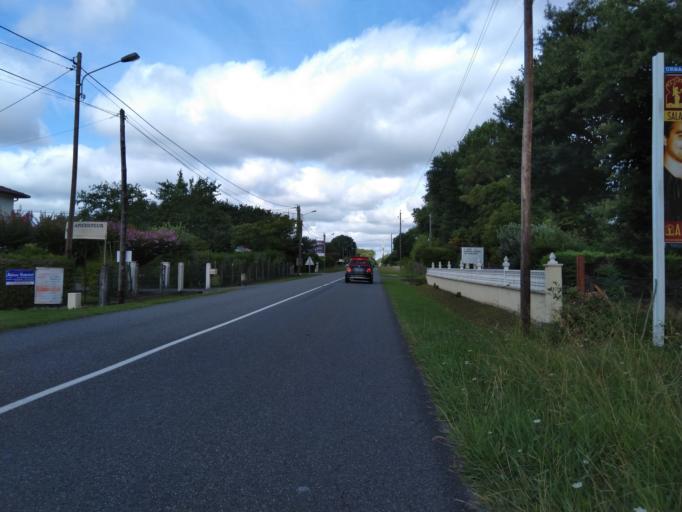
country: FR
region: Aquitaine
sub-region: Departement des Landes
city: Mees
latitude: 43.7308
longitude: -1.0955
